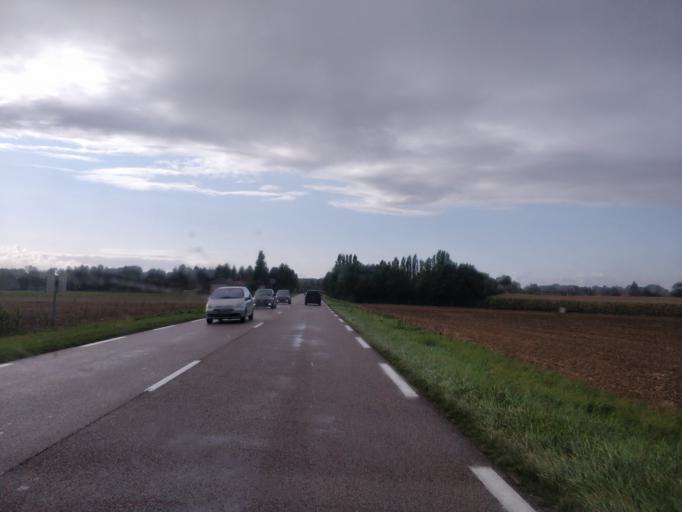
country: FR
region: Champagne-Ardenne
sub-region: Departement de l'Aube
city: Lusigny-sur-Barse
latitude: 48.2464
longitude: 4.2734
